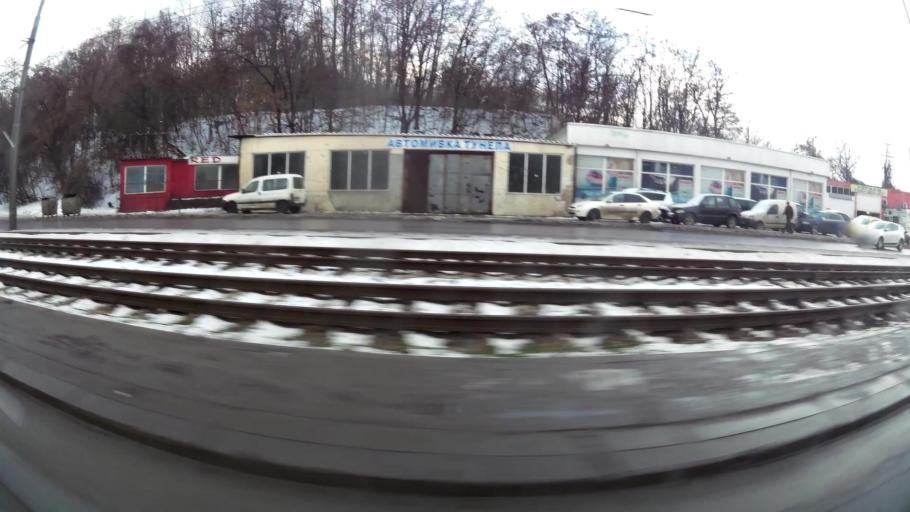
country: BG
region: Sofia-Capital
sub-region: Stolichna Obshtina
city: Sofia
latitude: 42.7098
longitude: 23.2731
